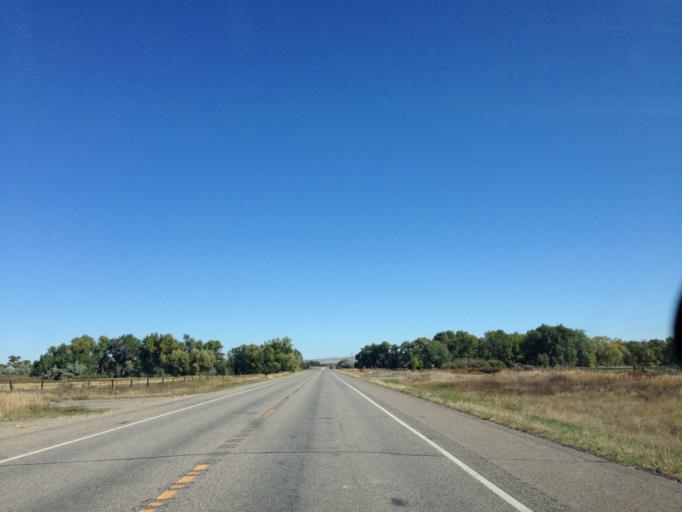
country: US
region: Montana
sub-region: Yellowstone County
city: Laurel
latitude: 45.4130
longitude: -108.8902
